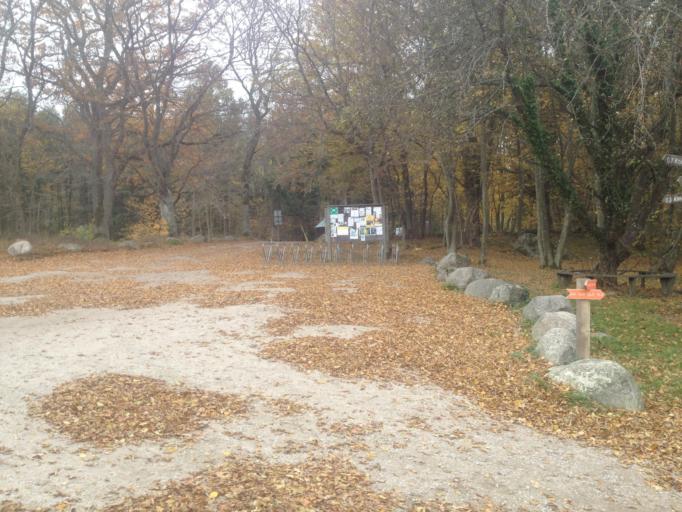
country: SE
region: Skane
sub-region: Simrishamns Kommun
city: Kivik
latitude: 55.6562
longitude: 14.2685
